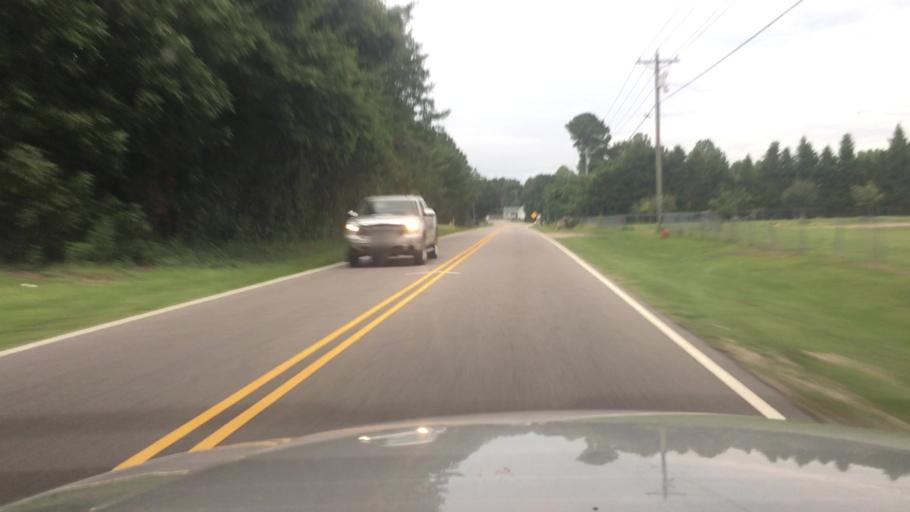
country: US
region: North Carolina
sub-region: Hoke County
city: Rockfish
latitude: 34.9640
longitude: -79.0529
